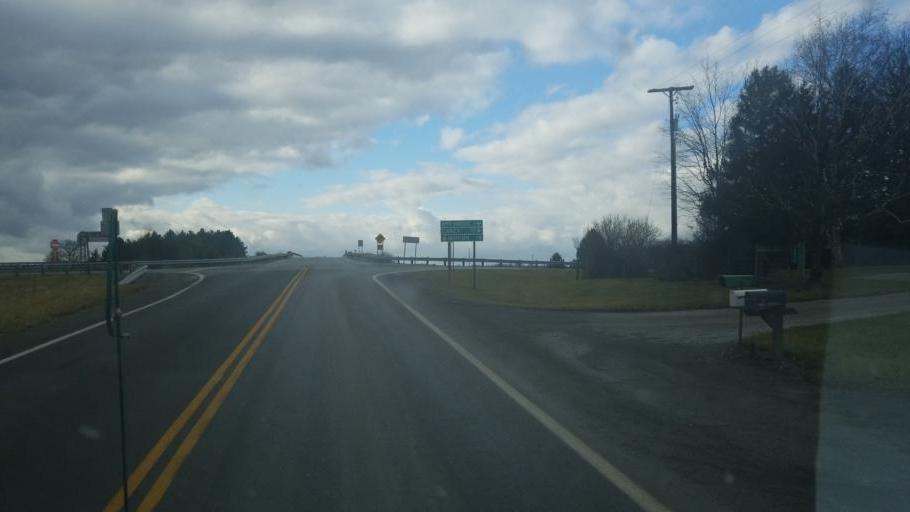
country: US
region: Ohio
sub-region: Wyandot County
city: Upper Sandusky
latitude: 40.7818
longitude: -83.2427
